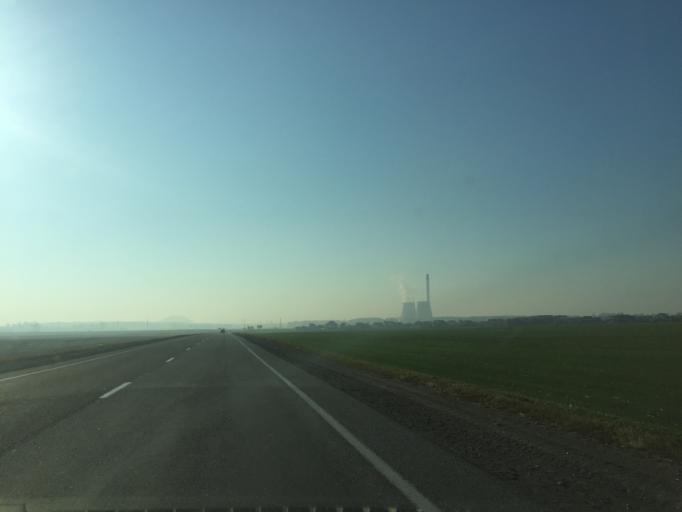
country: BY
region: Gomel
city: Kastsyukowka
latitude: 52.4702
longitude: 30.8234
